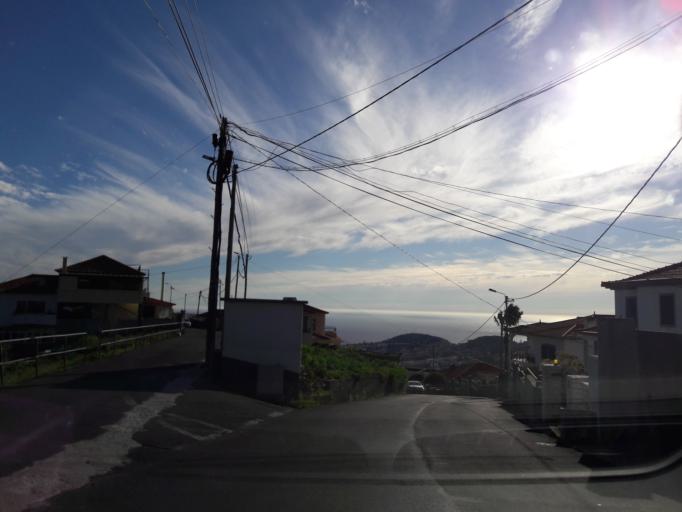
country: PT
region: Madeira
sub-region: Funchal
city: Nossa Senhora do Monte
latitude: 32.6754
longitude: -16.9205
